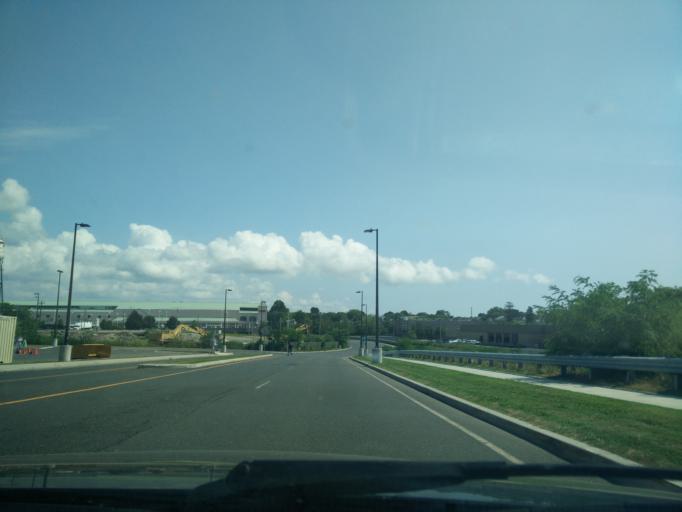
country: US
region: Connecticut
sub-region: Fairfield County
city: Bridgeport
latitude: 41.1596
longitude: -73.2331
